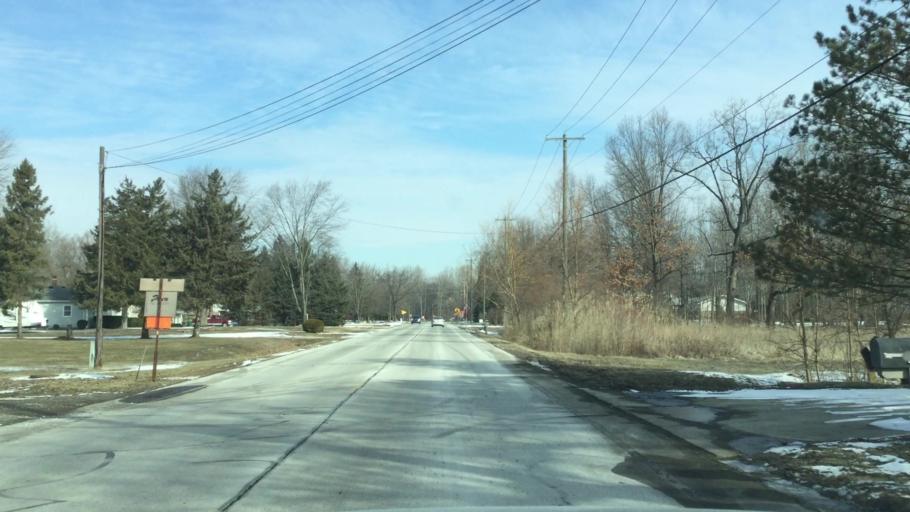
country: US
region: Michigan
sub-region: Wayne County
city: Flat Rock
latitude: 42.1344
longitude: -83.2900
